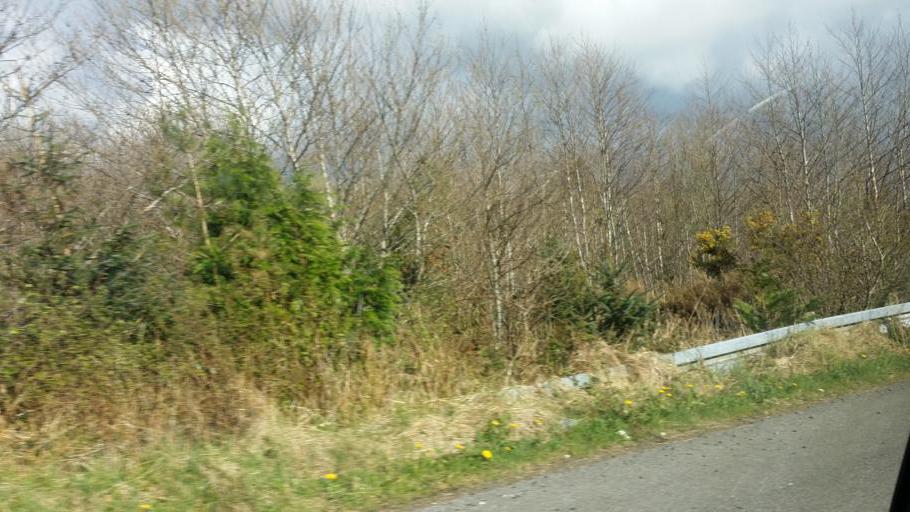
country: IE
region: Connaught
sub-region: County Leitrim
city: Manorhamilton
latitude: 54.3266
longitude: -8.2069
